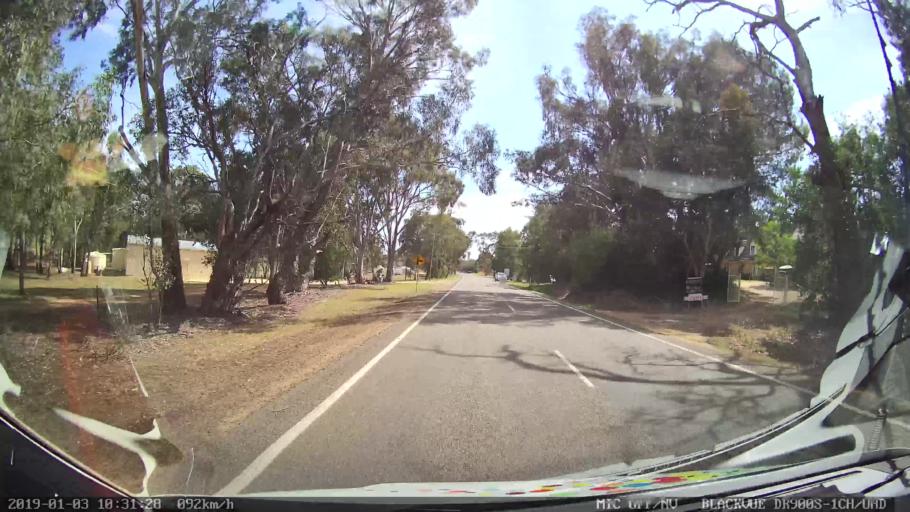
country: AU
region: New South Wales
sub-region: Young
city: Young
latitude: -34.3499
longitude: 148.2776
